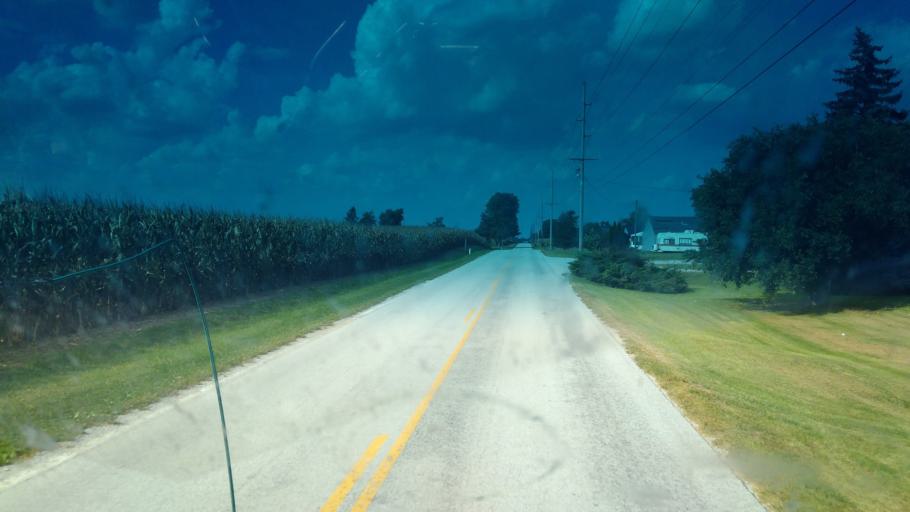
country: US
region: Ohio
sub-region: Hardin County
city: Kenton
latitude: 40.7552
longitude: -83.6524
